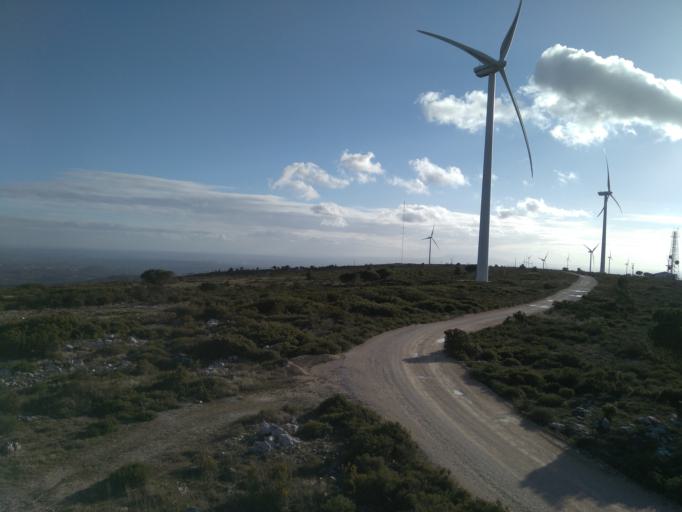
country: PT
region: Leiria
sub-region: Alcobaca
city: Benedita
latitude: 39.4374
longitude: -8.9187
